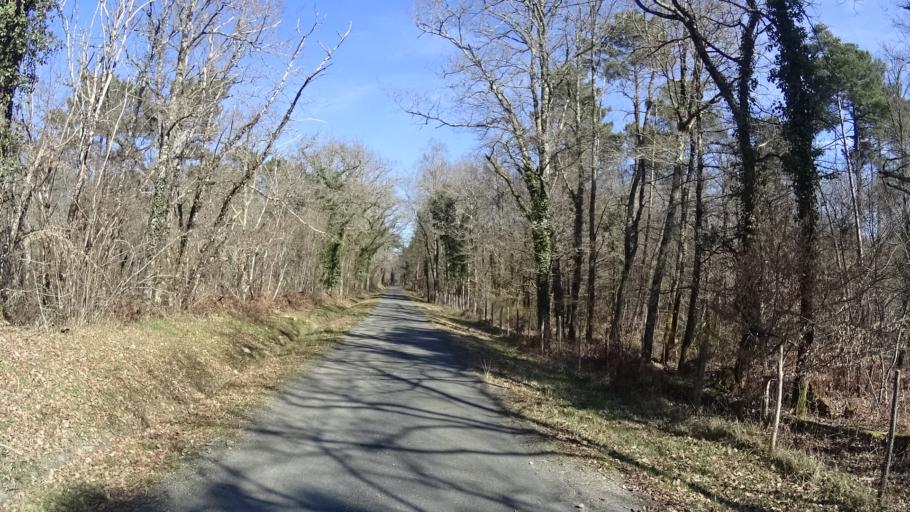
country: FR
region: Aquitaine
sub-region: Departement de la Dordogne
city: Riberac
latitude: 45.1828
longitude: 0.3018
